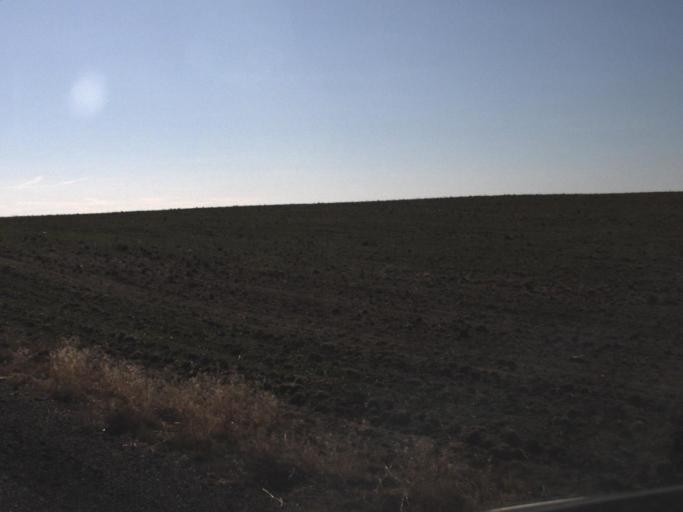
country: US
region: Washington
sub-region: Franklin County
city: Connell
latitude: 46.7612
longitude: -118.5476
